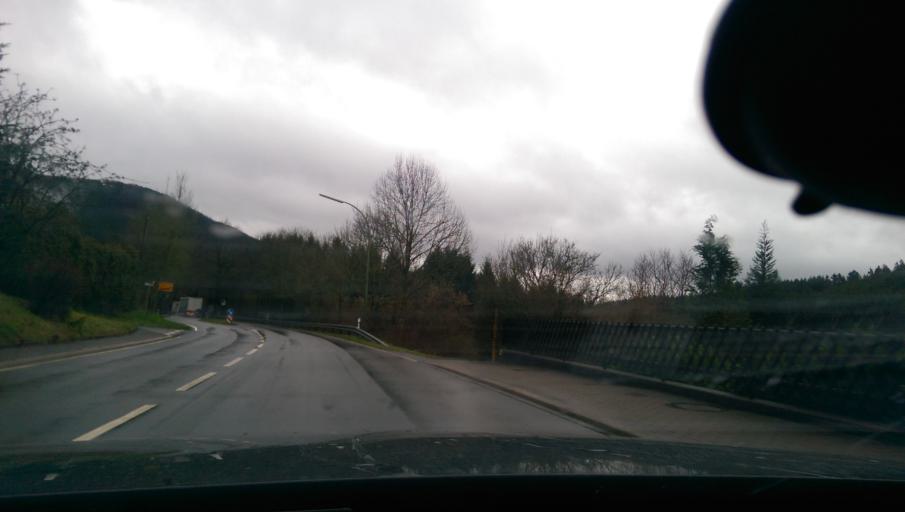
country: DE
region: North Rhine-Westphalia
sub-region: Regierungsbezirk Arnsberg
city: Finnentrop
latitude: 51.2128
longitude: 7.9640
